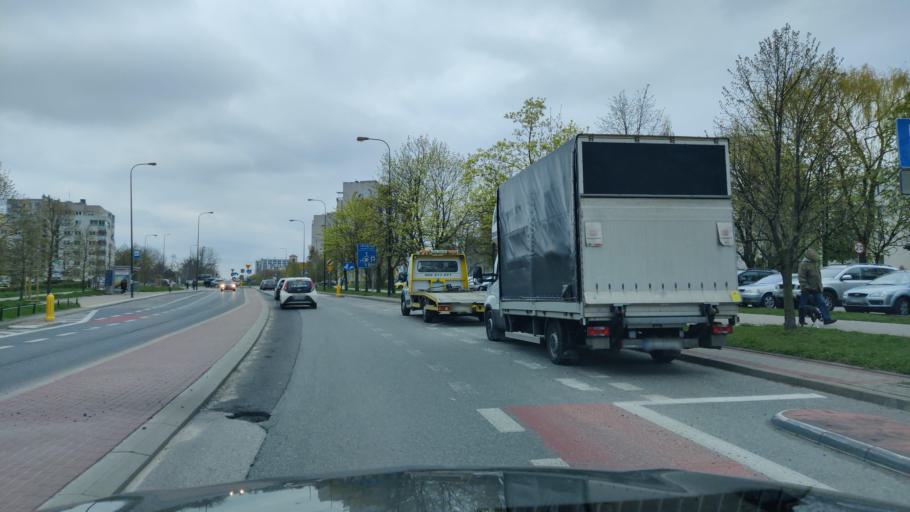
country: PL
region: Masovian Voivodeship
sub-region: Warszawa
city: Ursynow
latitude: 52.1434
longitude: 21.0440
